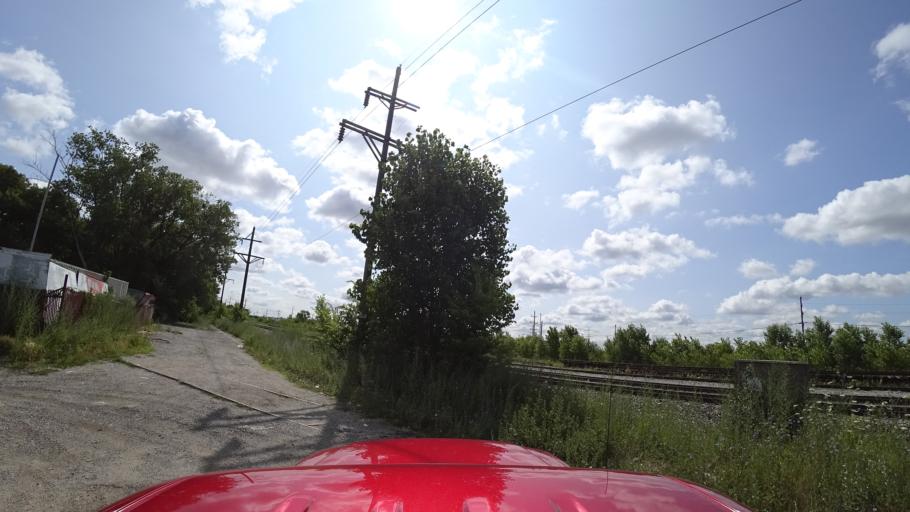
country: US
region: Illinois
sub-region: Cook County
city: Cicero
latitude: 41.8331
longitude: -87.7328
